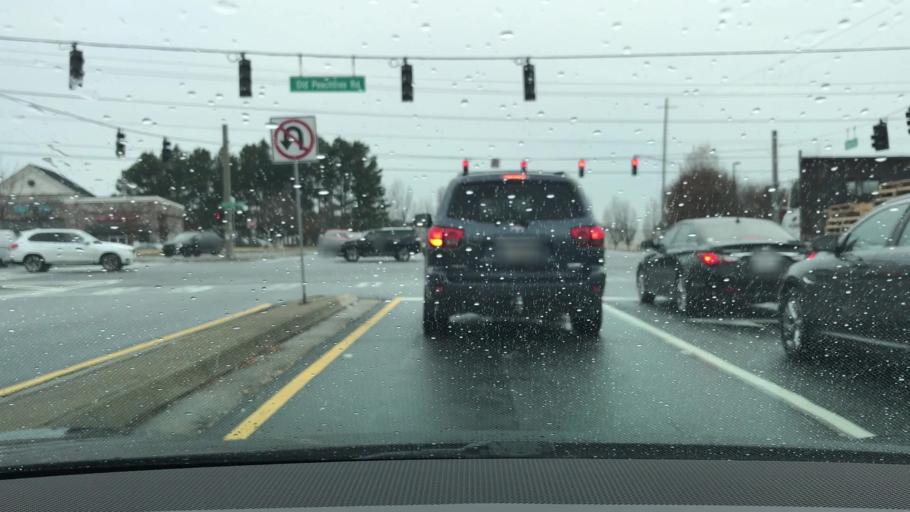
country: US
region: Georgia
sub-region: Gwinnett County
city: Suwanee
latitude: 34.0026
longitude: -84.0806
